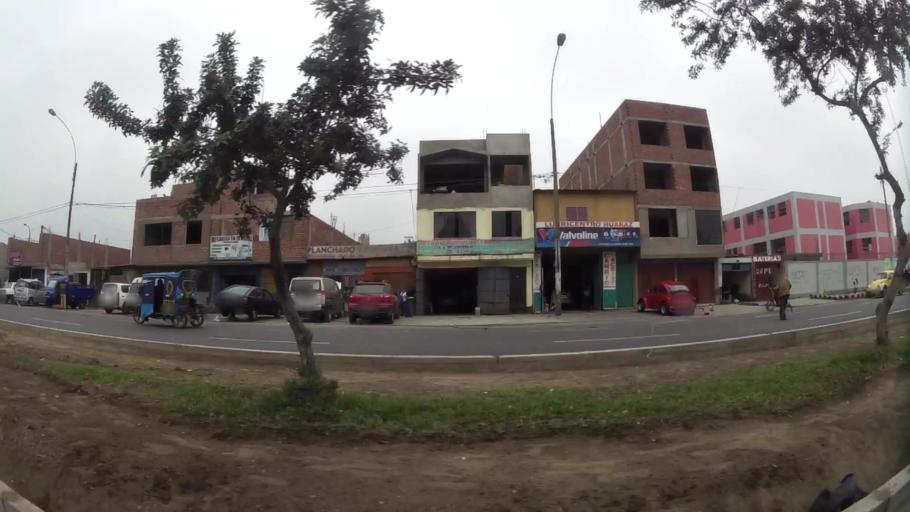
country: PE
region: Lima
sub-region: Lima
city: Independencia
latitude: -11.9629
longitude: -77.0771
